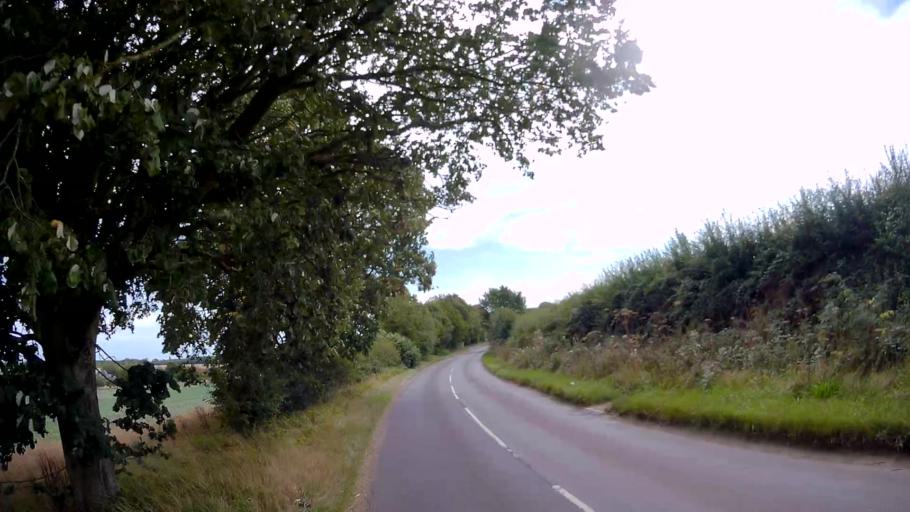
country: GB
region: England
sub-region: Hampshire
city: Long Sutton
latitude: 51.2230
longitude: -0.9470
